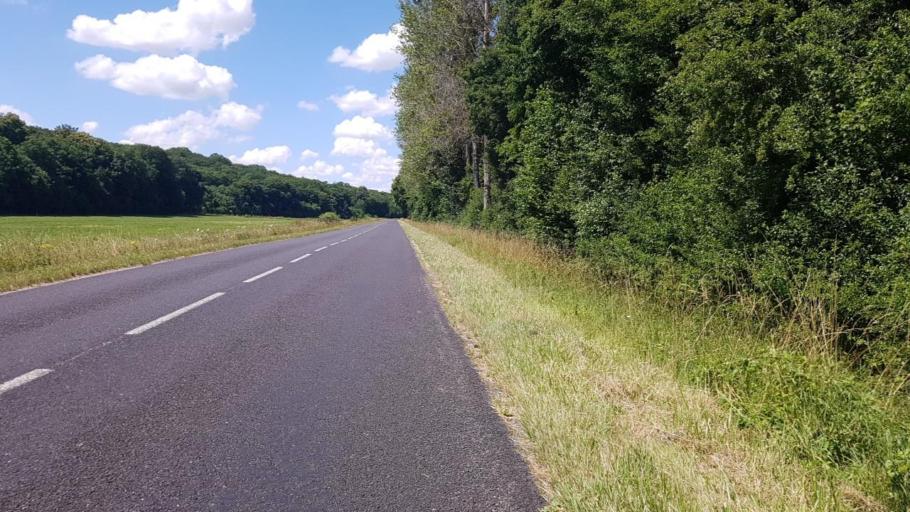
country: FR
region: Lorraine
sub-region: Departement de la Meuse
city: Vacon
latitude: 48.6718
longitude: 5.5722
